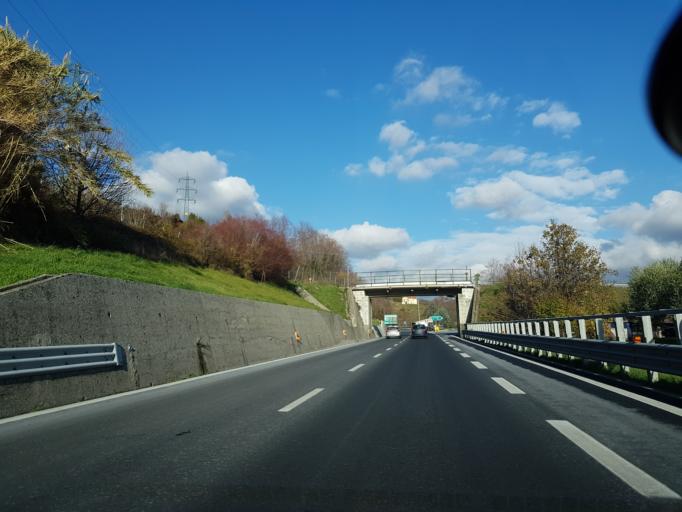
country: IT
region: Liguria
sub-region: Provincia di Genova
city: Pedemonte
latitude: 44.5018
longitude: 8.9181
